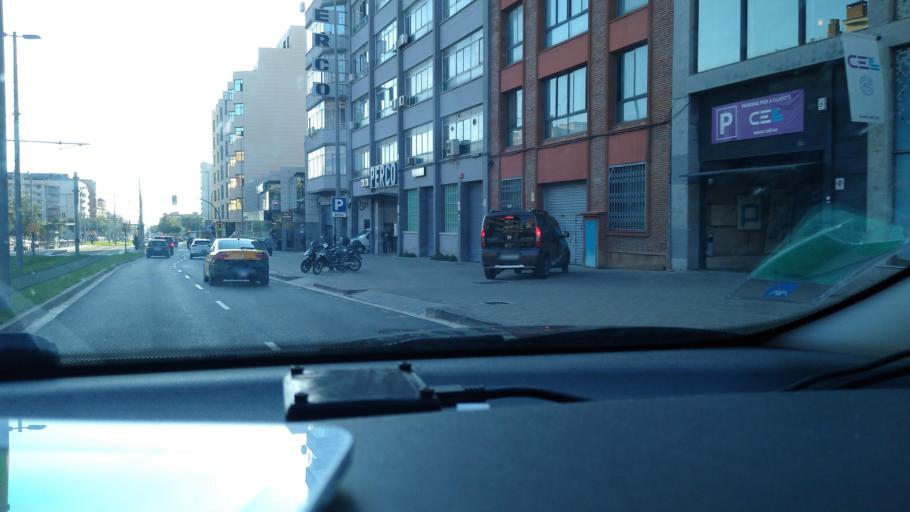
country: ES
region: Catalonia
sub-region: Provincia de Barcelona
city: Esplugues de Llobregat
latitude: 41.3704
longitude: 2.0817
